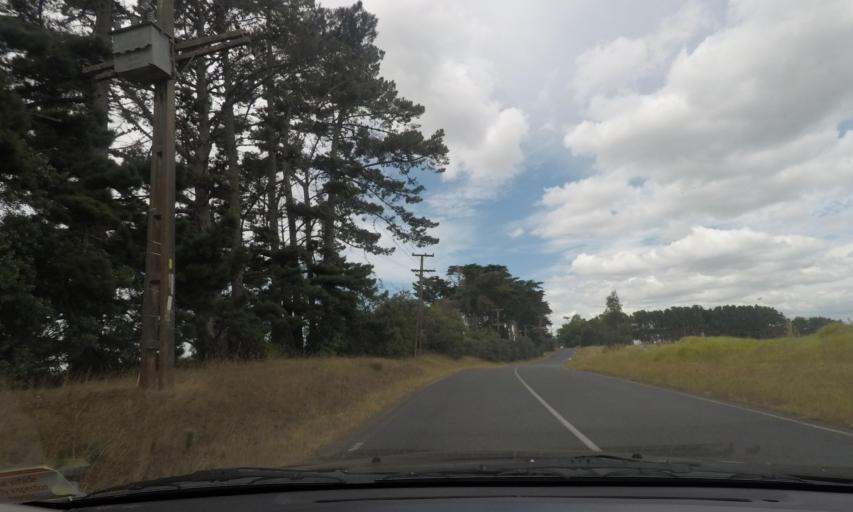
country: NZ
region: Auckland
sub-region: Auckland
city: Mangere
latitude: -36.9938
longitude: 174.7703
